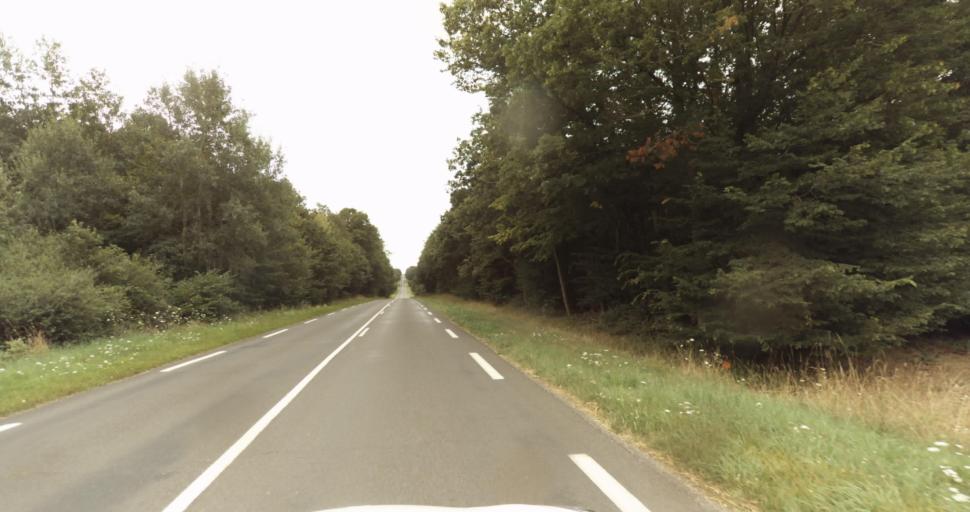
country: FR
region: Haute-Normandie
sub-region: Departement de l'Eure
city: La Madeleine-de-Nonancourt
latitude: 48.8175
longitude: 1.1868
